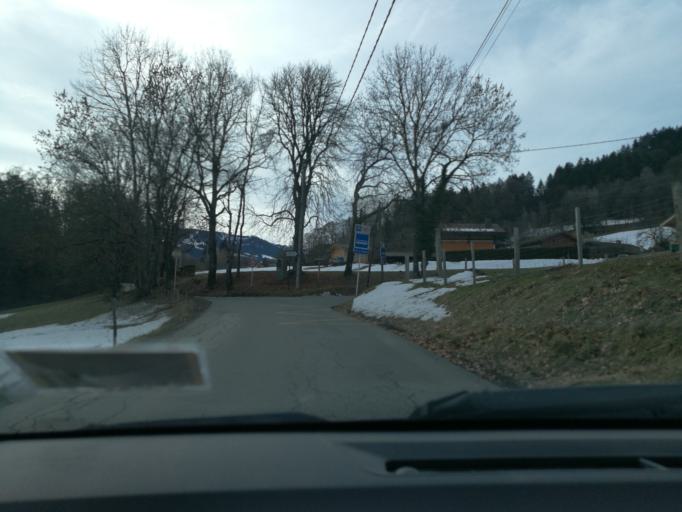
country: FR
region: Rhone-Alpes
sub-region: Departement de la Haute-Savoie
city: Cordon
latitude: 45.9187
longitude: 6.6286
